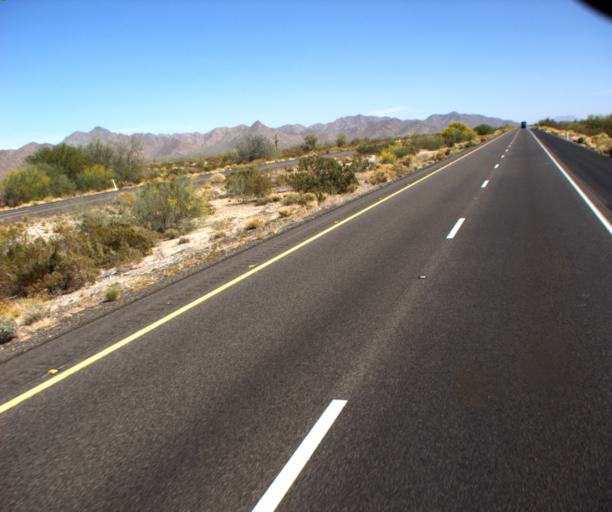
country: US
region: Arizona
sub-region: Maricopa County
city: Gila Bend
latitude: 32.8906
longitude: -112.4846
